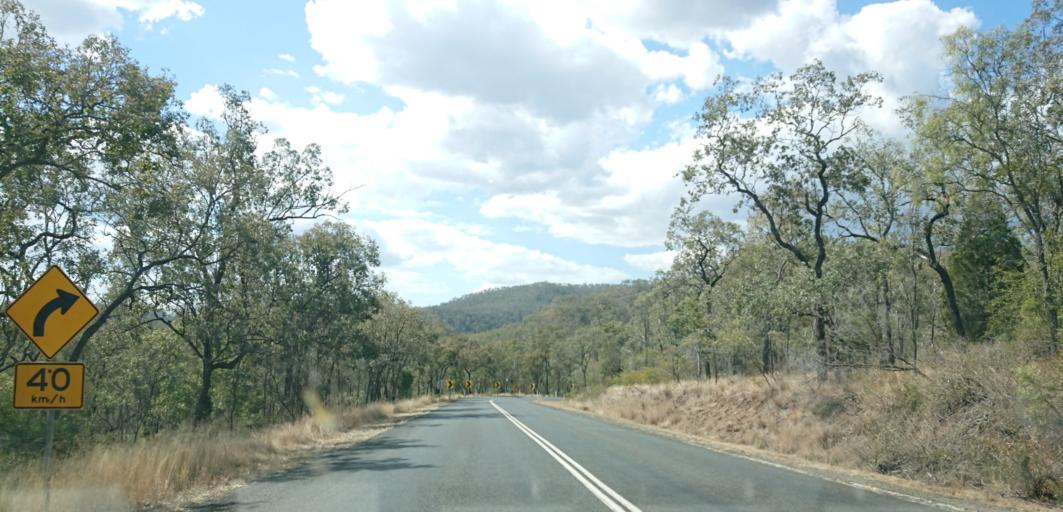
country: AU
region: Queensland
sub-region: Toowoomba
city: Top Camp
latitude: -27.8169
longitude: 152.1051
